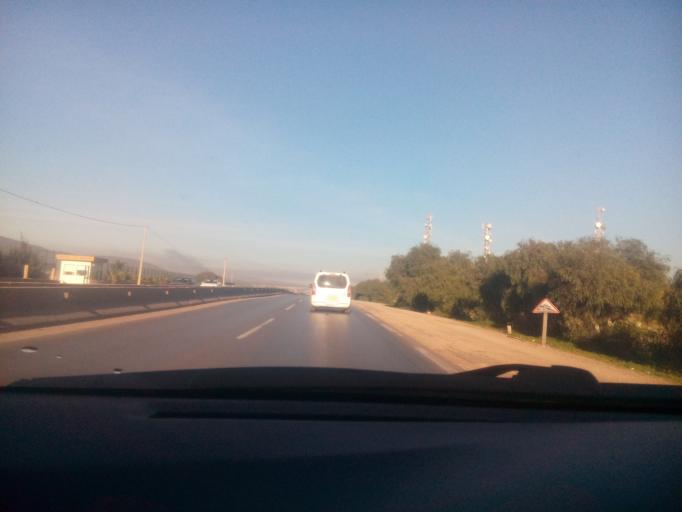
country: DZ
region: Oran
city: Bir el Djir
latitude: 35.7518
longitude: -0.4857
